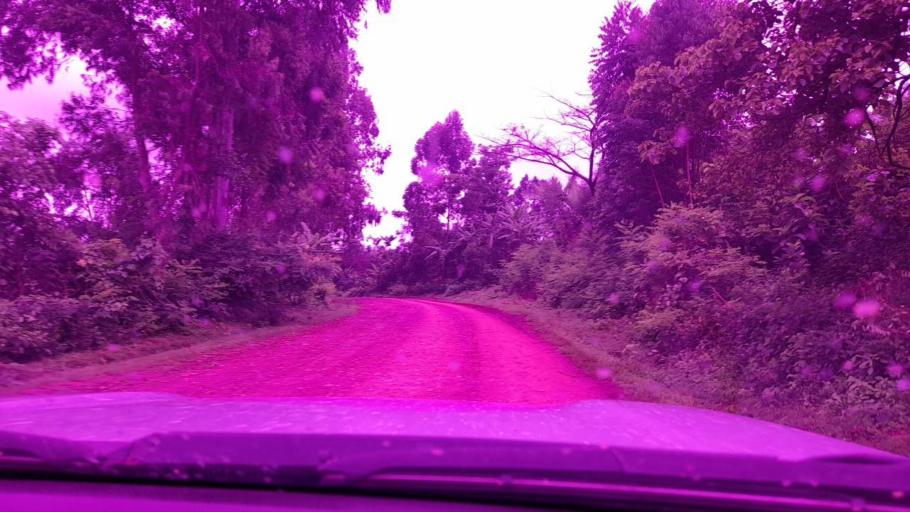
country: ET
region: Southern Nations, Nationalities, and People's Region
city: Bonga
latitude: 7.5500
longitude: 35.8726
